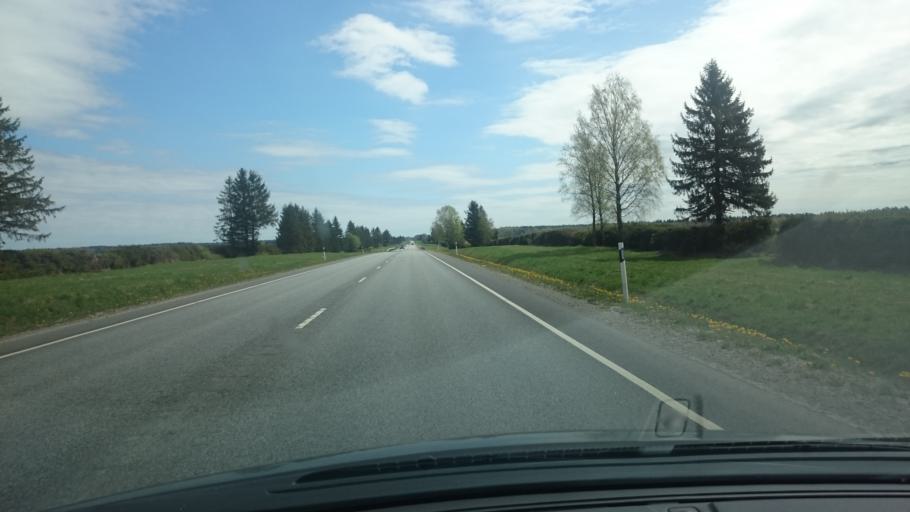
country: EE
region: Laeaene-Virumaa
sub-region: Someru vald
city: Someru
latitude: 59.3660
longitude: 26.4685
